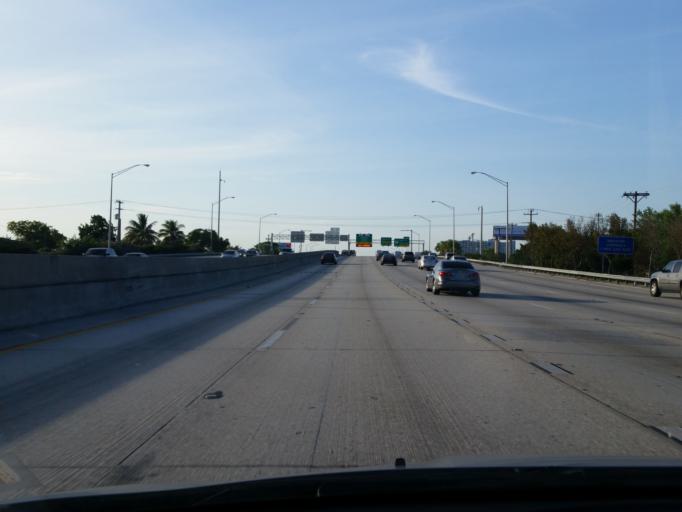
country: US
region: Florida
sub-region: Miami-Dade County
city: Allapattah
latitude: 25.8015
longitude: -80.2055
